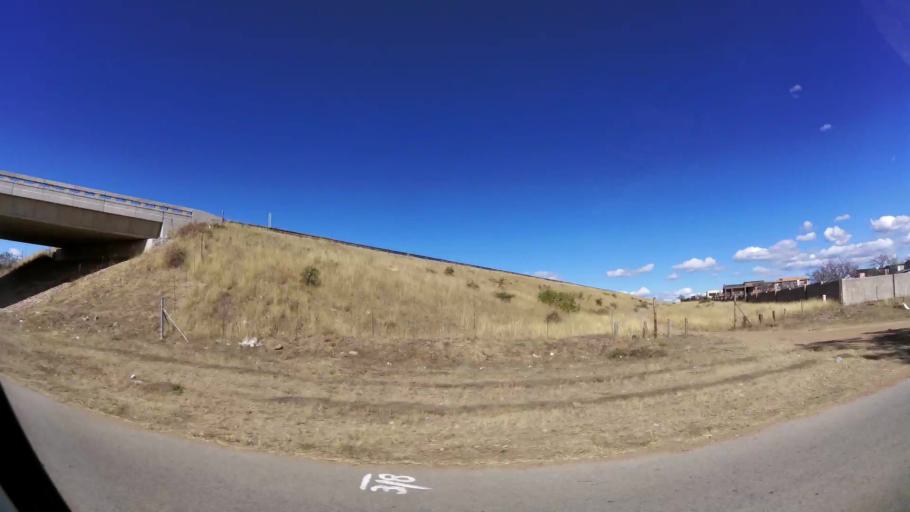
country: ZA
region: Limpopo
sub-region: Capricorn District Municipality
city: Polokwane
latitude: -23.8586
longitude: 29.5056
